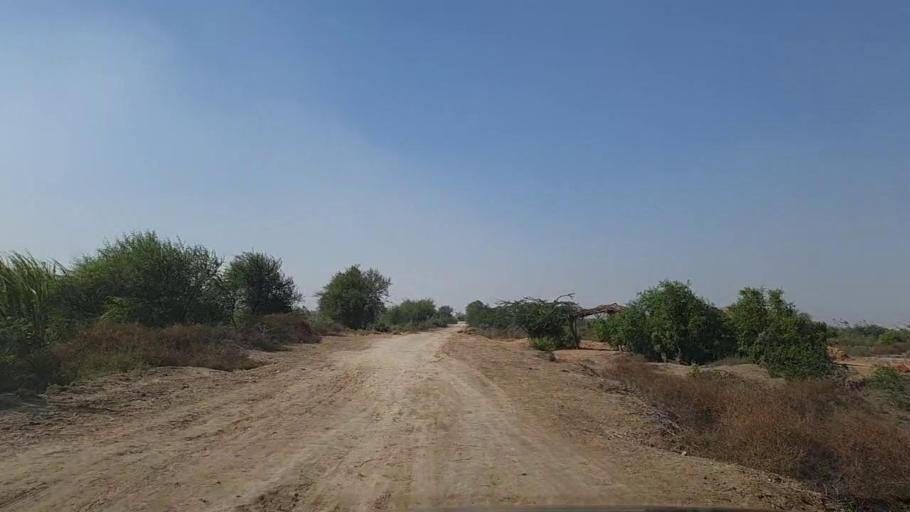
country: PK
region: Sindh
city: Daro Mehar
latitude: 24.8382
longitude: 68.1357
